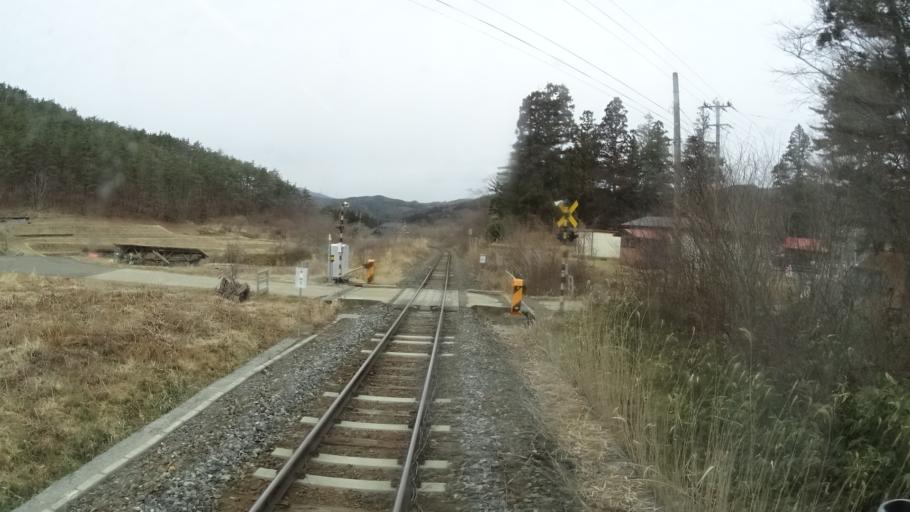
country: JP
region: Iwate
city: Tono
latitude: 39.3422
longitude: 141.3537
